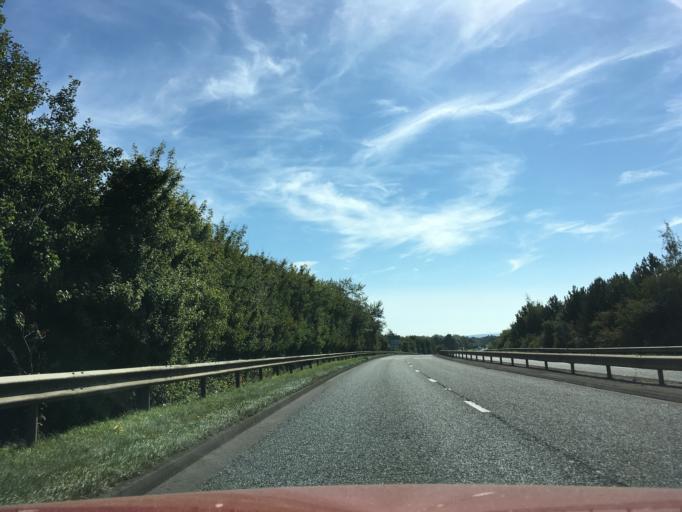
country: GB
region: England
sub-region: South Gloucestershire
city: Severn Beach
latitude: 51.5678
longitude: -2.6431
